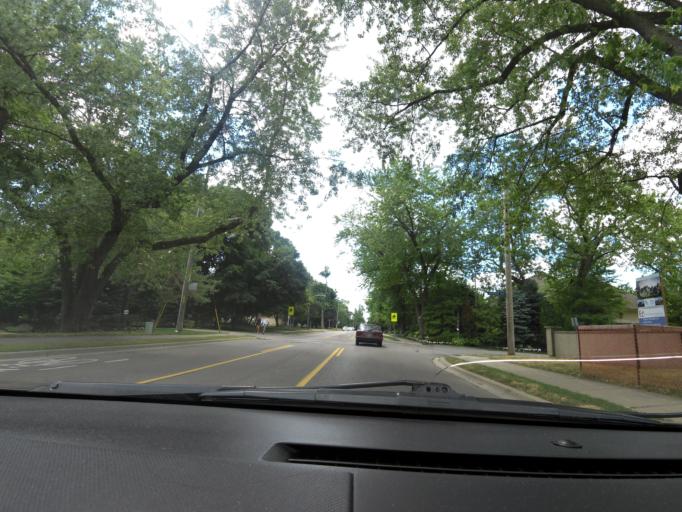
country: CA
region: Ontario
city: Burlington
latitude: 43.3431
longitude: -79.7652
